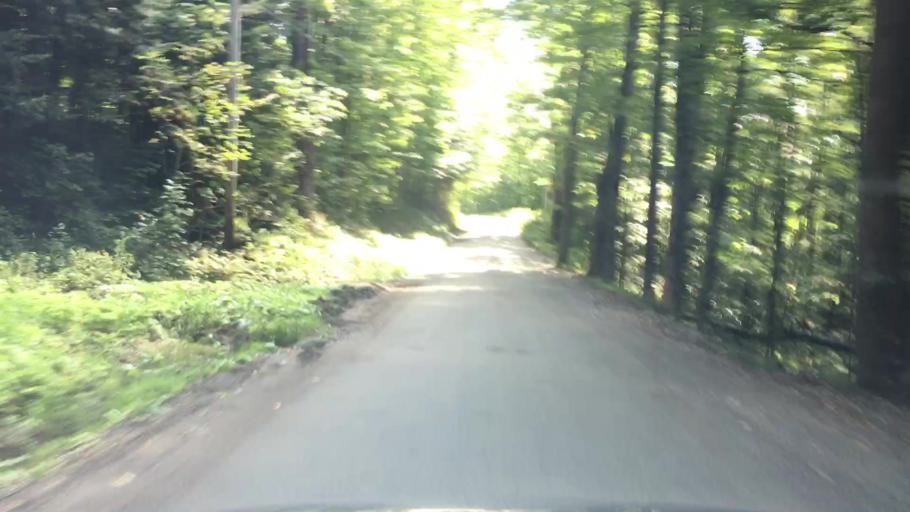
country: US
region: Vermont
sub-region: Windham County
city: West Brattleboro
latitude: 42.7968
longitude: -72.6354
